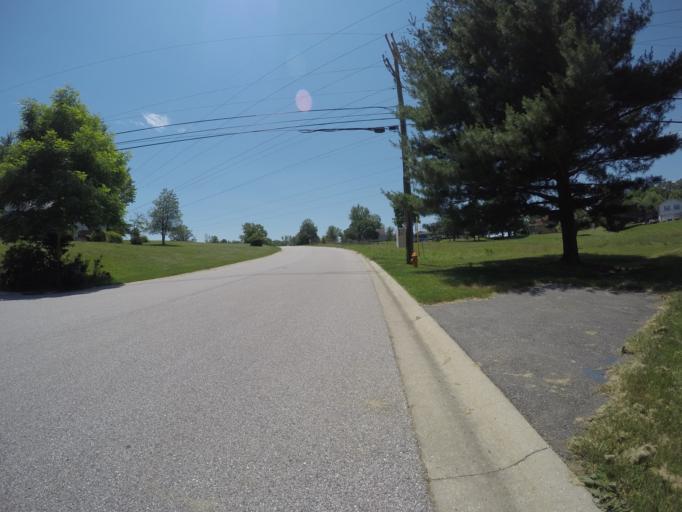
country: US
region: Maryland
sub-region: Howard County
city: Ilchester
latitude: 39.2367
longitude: -76.7871
